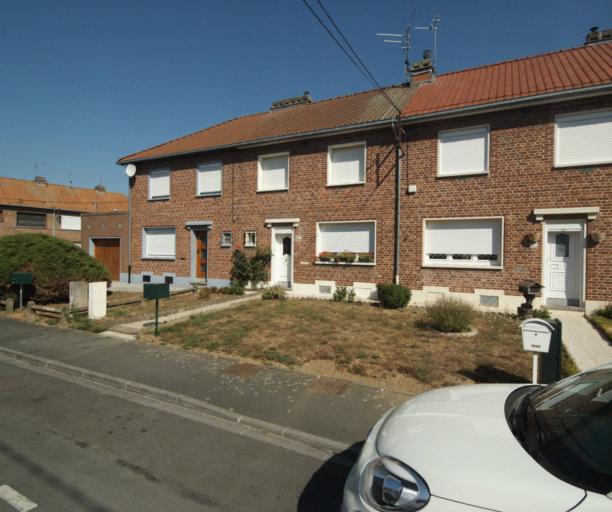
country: FR
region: Nord-Pas-de-Calais
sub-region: Departement du Nord
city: Wervicq-Sud
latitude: 50.7687
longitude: 3.0455
